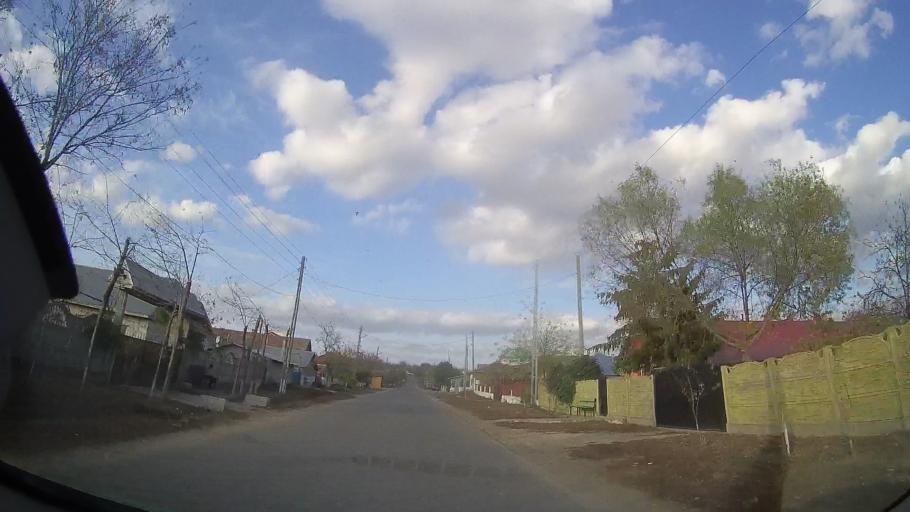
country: RO
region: Constanta
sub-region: Comuna Cerchezu
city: Cerchezu
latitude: 43.8568
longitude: 28.1013
